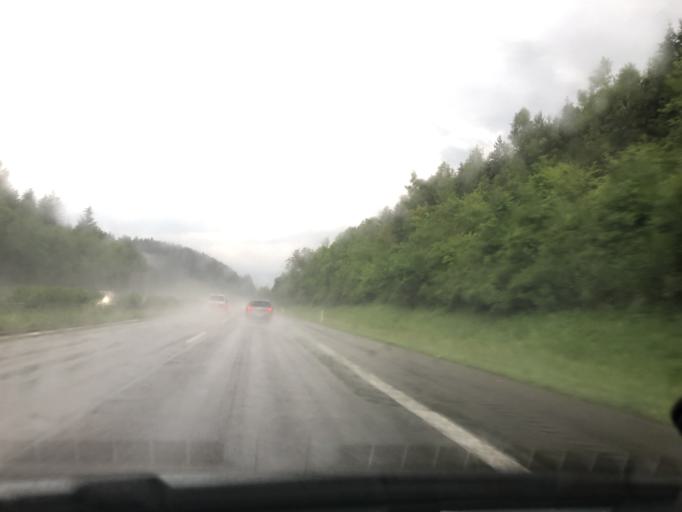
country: DE
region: Baden-Wuerttemberg
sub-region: Freiburg Region
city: Vohringen
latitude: 48.2912
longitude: 8.6369
